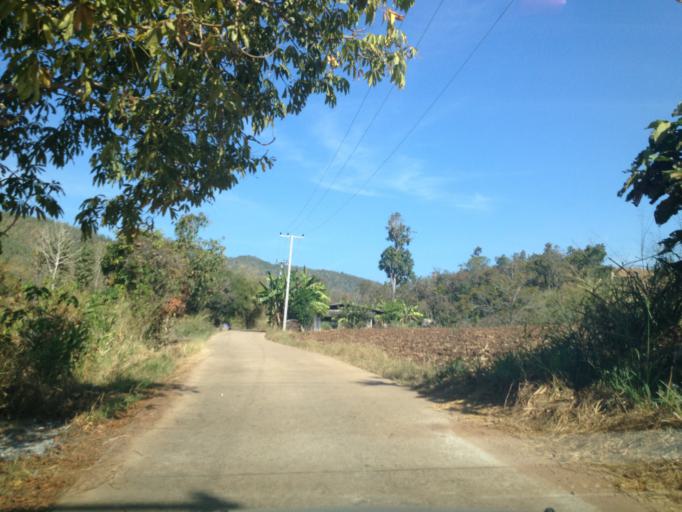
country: TH
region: Mae Hong Son
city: Ban Huai I Huak
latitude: 18.0703
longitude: 98.1834
